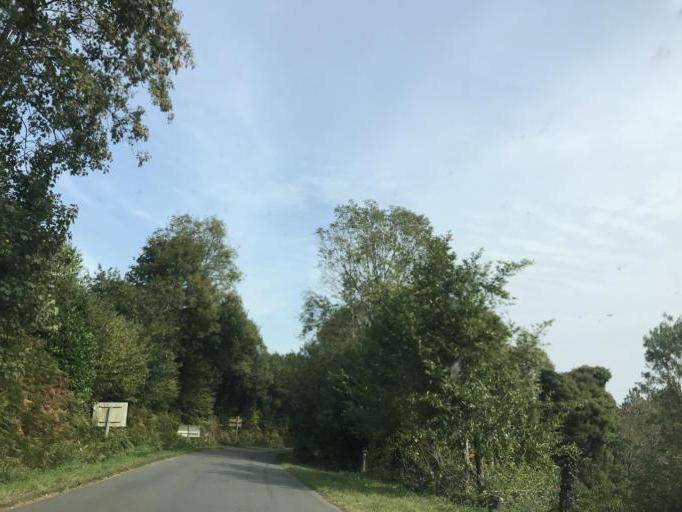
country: FR
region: Brittany
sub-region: Departement du Finistere
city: Brasparts
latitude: 48.3032
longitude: -3.9511
